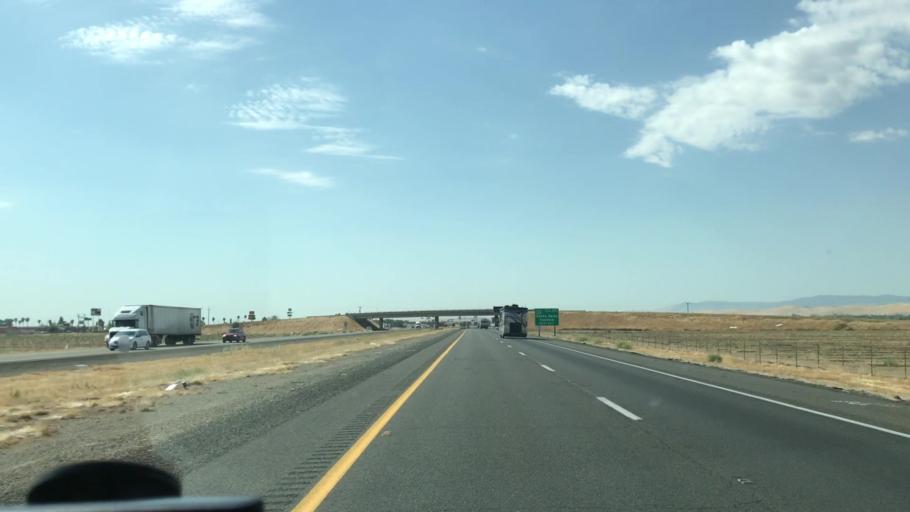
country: US
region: California
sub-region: Merced County
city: Gustine
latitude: 37.1181
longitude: -121.0247
